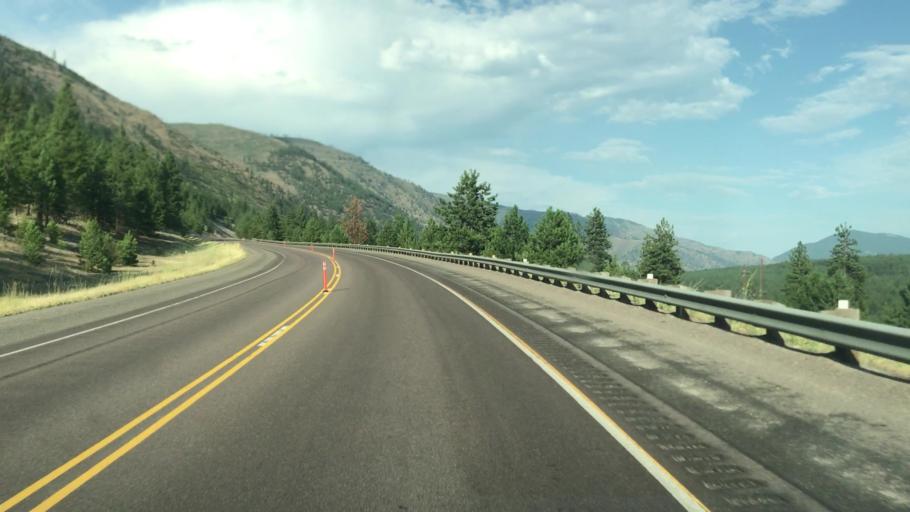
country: US
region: Montana
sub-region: Mineral County
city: Superior
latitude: 47.0136
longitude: -114.6959
